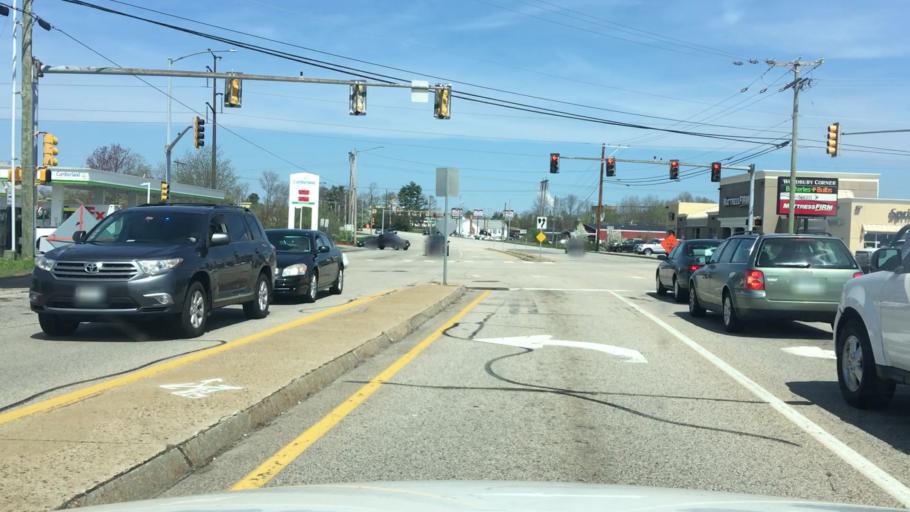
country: US
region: Maine
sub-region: York County
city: South Eliot
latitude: 43.0939
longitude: -70.7939
